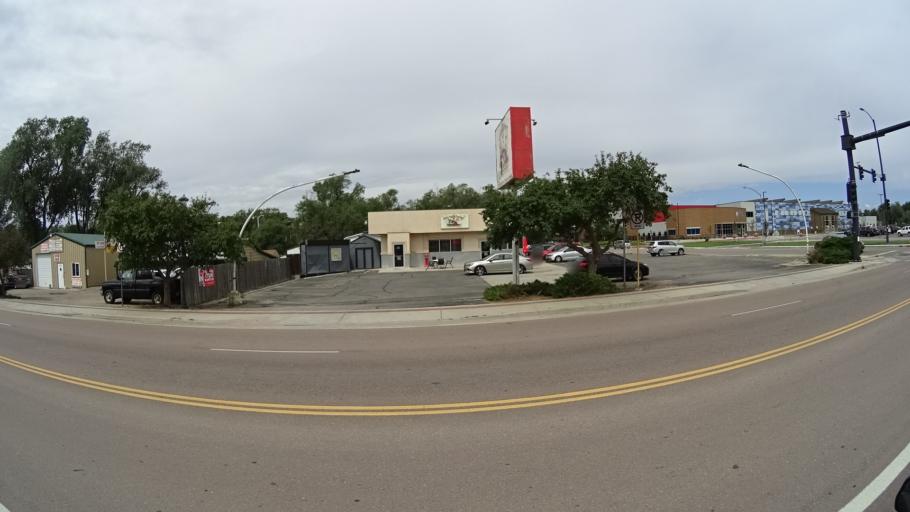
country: US
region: Colorado
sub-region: El Paso County
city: Fountain
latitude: 38.6851
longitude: -104.7041
